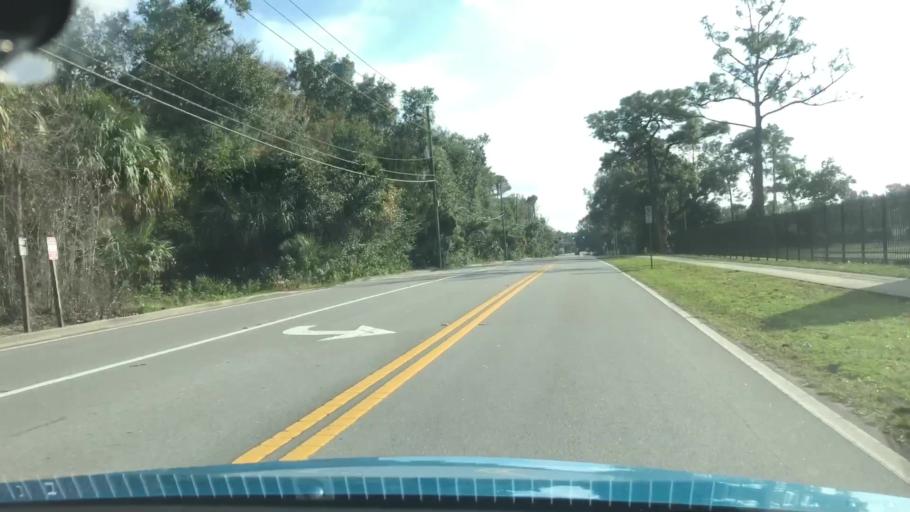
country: US
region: Florida
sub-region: Seminole County
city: Lake Mary
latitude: 28.7361
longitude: -81.3343
